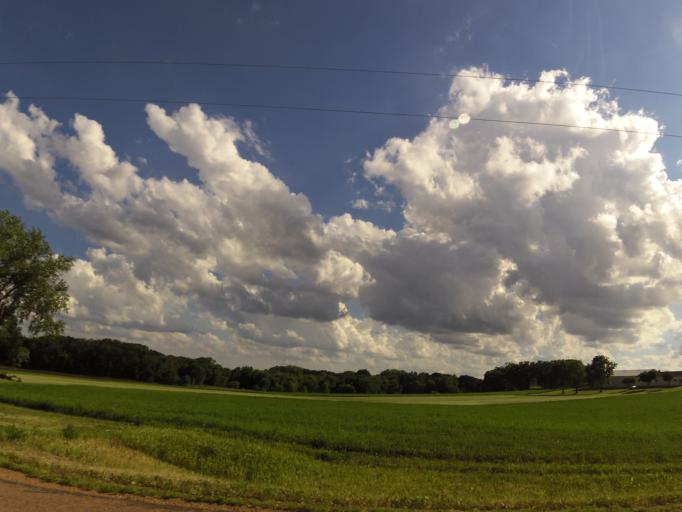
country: US
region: Minnesota
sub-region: Carver County
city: Victoria
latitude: 44.8086
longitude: -93.6593
